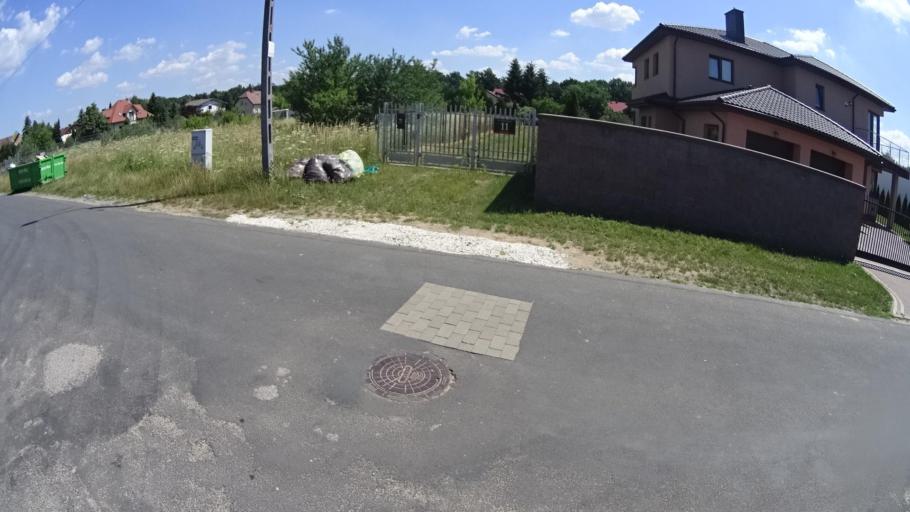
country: PL
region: Masovian Voivodeship
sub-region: Powiat warszawski zachodni
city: Babice
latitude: 52.2590
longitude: 20.8494
